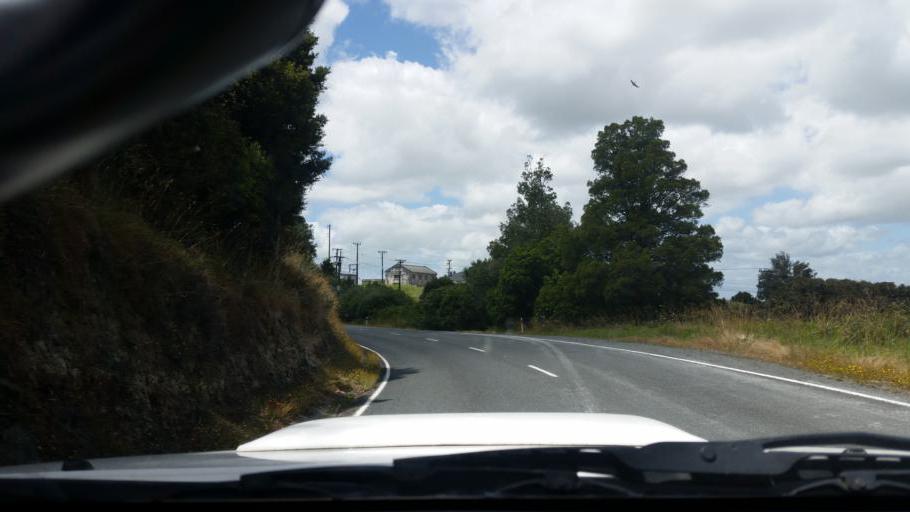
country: NZ
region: Northland
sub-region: Whangarei
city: Ruakaka
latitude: -36.0717
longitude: 174.2645
